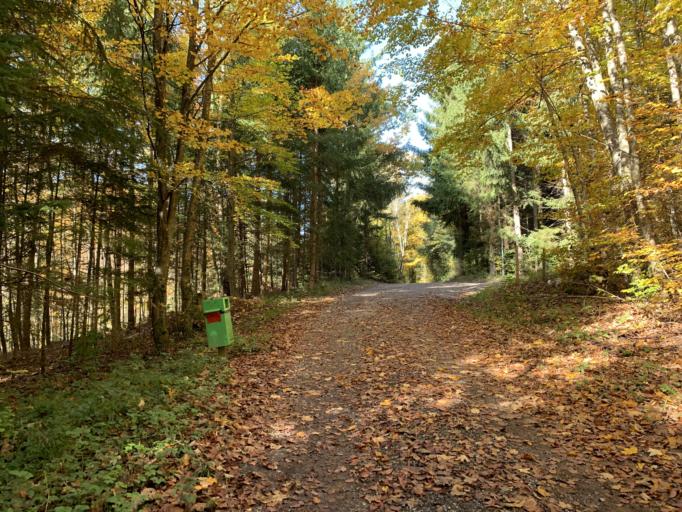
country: CH
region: Zurich
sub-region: Bezirk Hinwil
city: Hinwil
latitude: 47.3100
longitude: 8.8548
